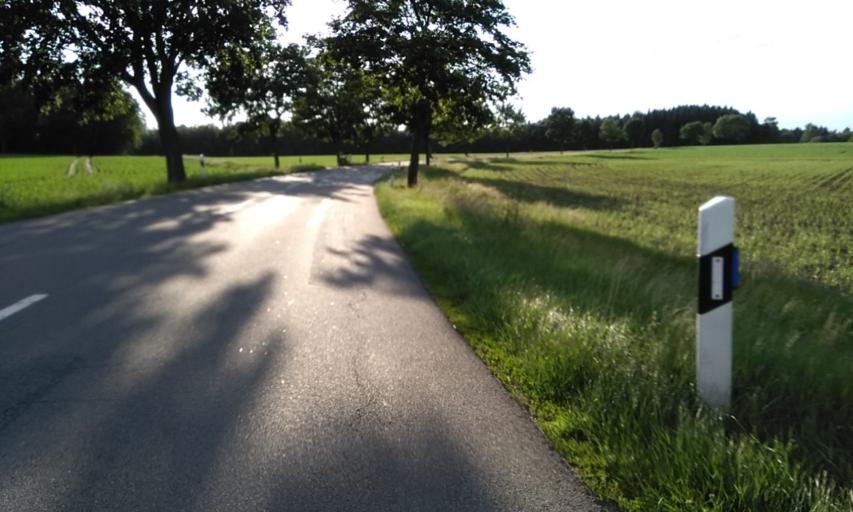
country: DE
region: Lower Saxony
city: Heeslingen
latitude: 53.3521
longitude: 9.3474
